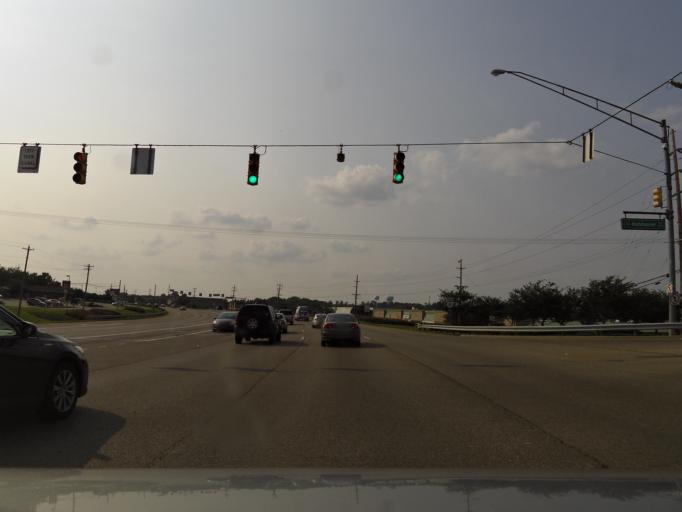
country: US
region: Ohio
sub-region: Hamilton County
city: Springdale
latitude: 39.3145
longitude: -84.4878
